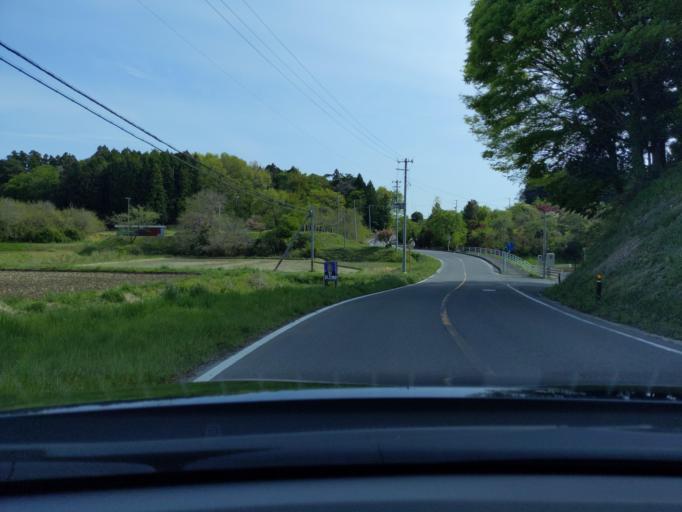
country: JP
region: Fukushima
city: Koriyama
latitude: 37.3603
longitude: 140.4190
